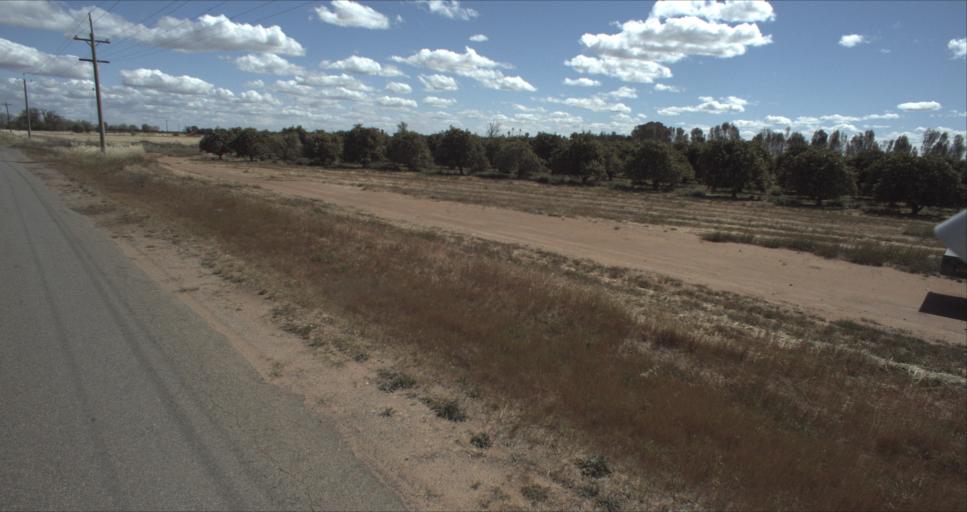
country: AU
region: New South Wales
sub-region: Leeton
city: Leeton
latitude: -34.5112
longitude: 146.2531
